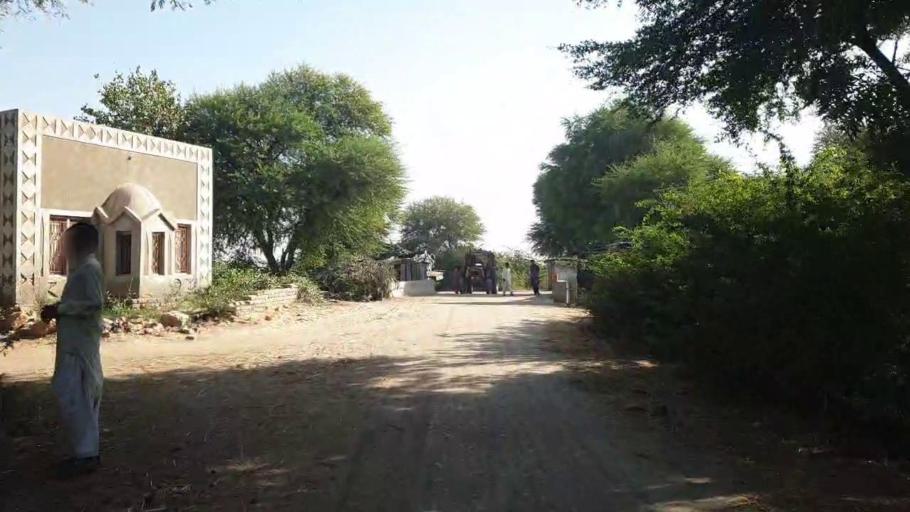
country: PK
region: Sindh
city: Matli
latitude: 25.0099
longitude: 68.7404
